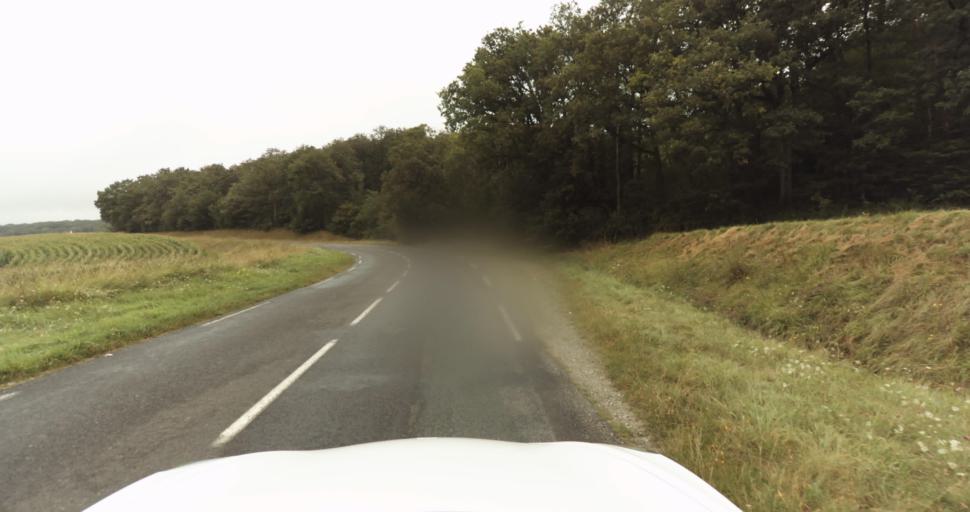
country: FR
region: Haute-Normandie
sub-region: Departement de l'Eure
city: Normanville
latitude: 49.0738
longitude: 1.1731
